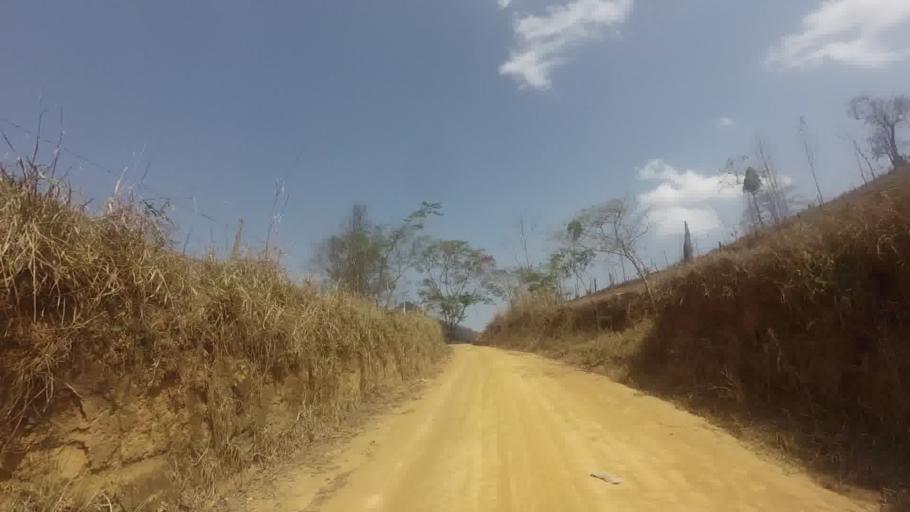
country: BR
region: Espirito Santo
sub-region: Sao Jose Do Calcado
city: Sao Jose do Calcado
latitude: -21.0425
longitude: -41.5269
